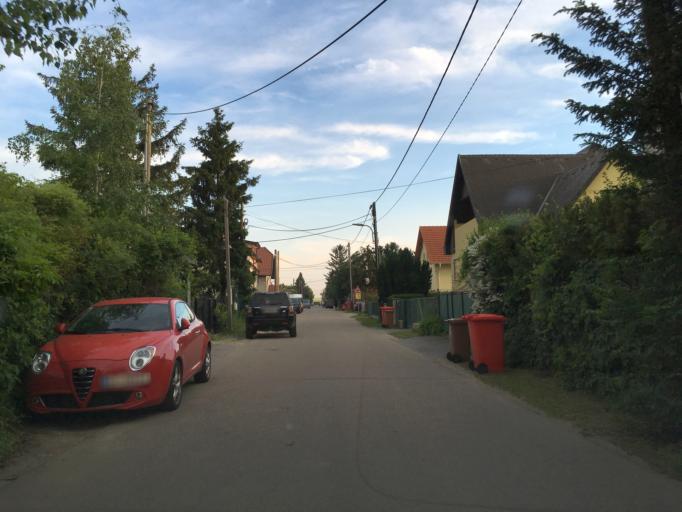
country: AT
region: Lower Austria
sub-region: Politischer Bezirk Wien-Umgebung
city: Gerasdorf bei Wien
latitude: 48.3146
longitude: 16.4948
